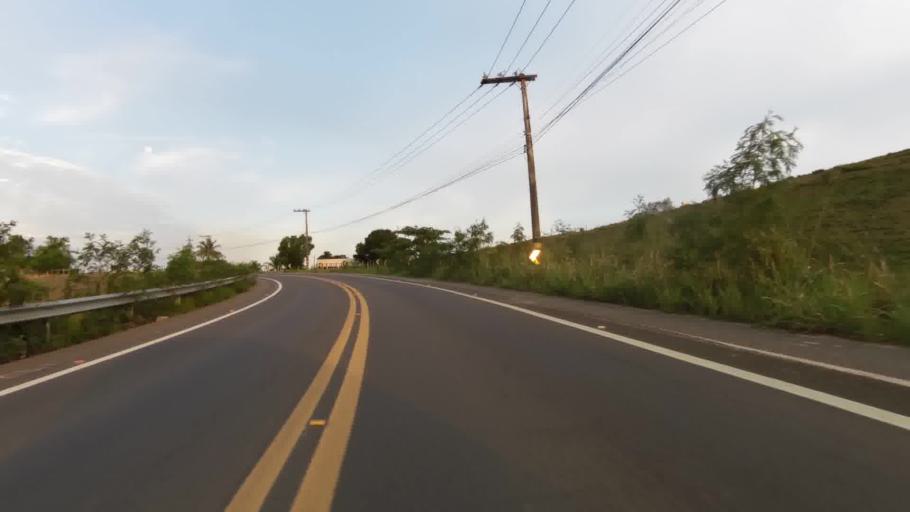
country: BR
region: Espirito Santo
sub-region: Piuma
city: Piuma
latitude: -20.8059
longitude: -40.6705
